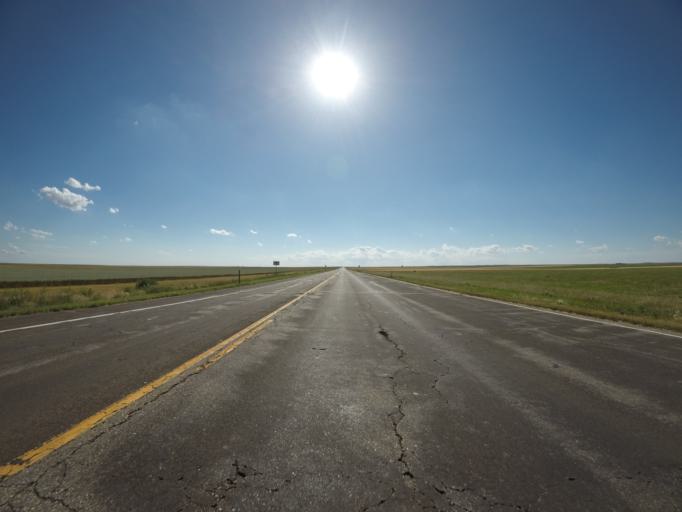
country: US
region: Colorado
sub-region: Logan County
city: Sterling
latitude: 40.6240
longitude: -103.3568
